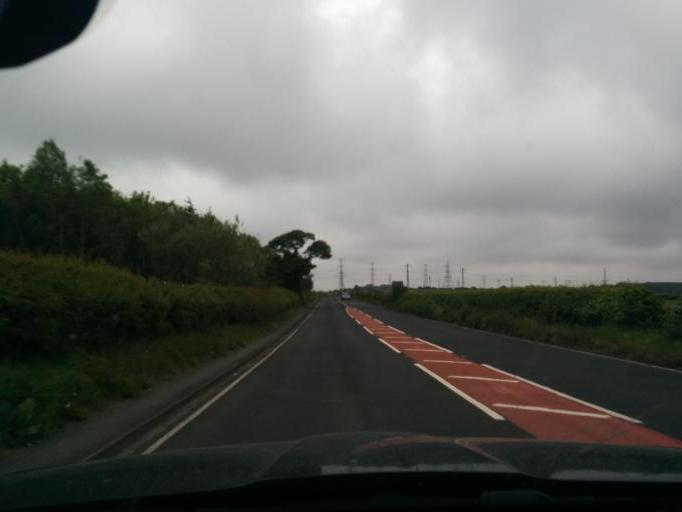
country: GB
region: England
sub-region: Northumberland
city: Bedlington
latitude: 55.1220
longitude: -1.5774
